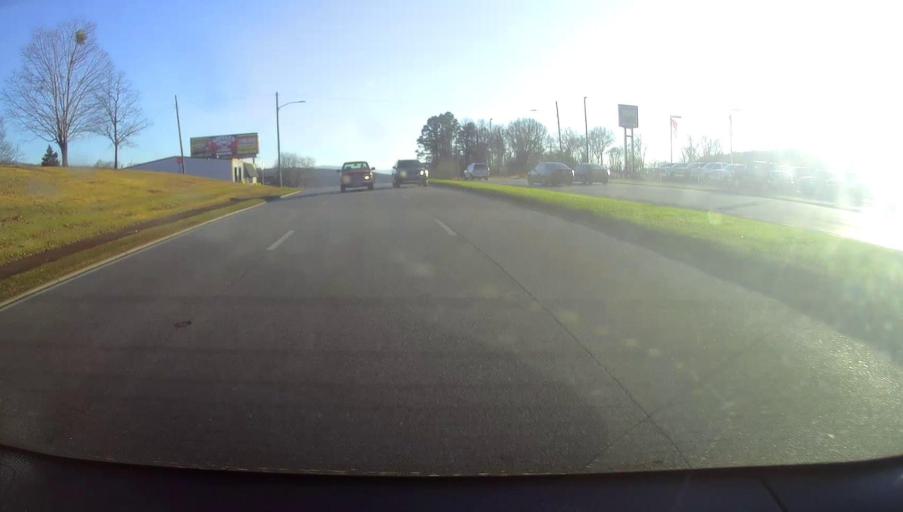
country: US
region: Alabama
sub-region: Calhoun County
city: Anniston
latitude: 33.6500
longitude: -85.8265
